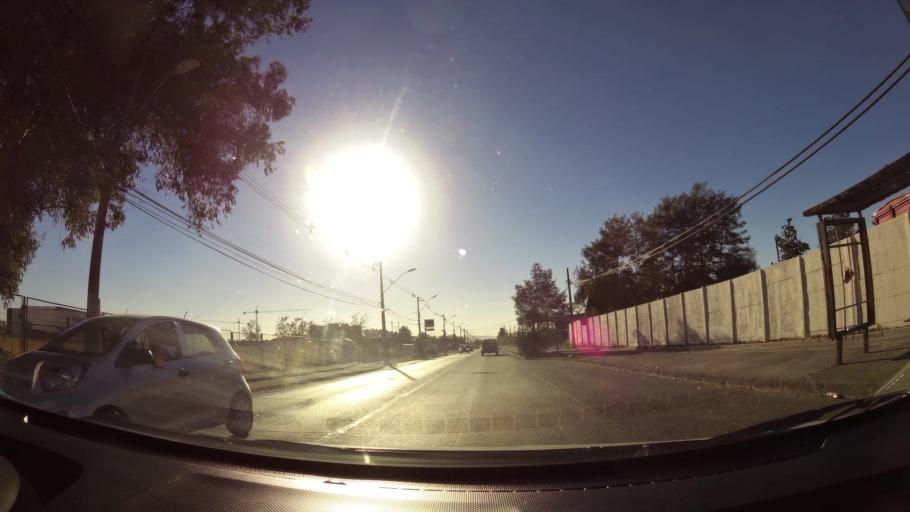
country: CL
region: Maule
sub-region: Provincia de Curico
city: Curico
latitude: -34.9773
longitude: -71.2087
